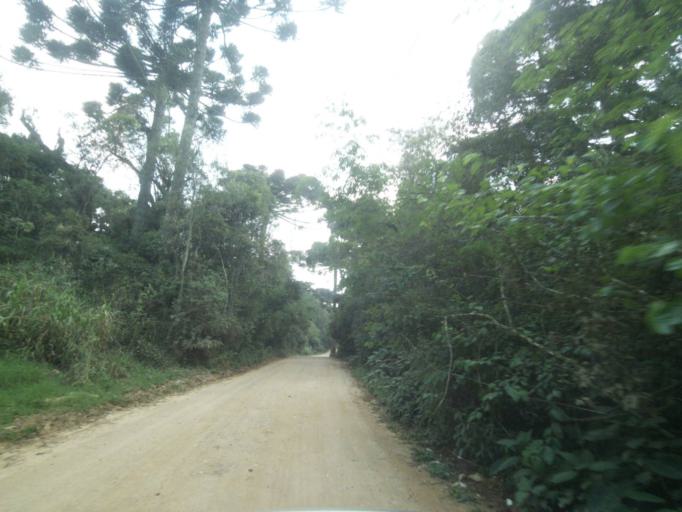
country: BR
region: Parana
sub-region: Sao Jose Dos Pinhais
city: Sao Jose dos Pinhais
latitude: -25.5423
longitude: -49.2341
